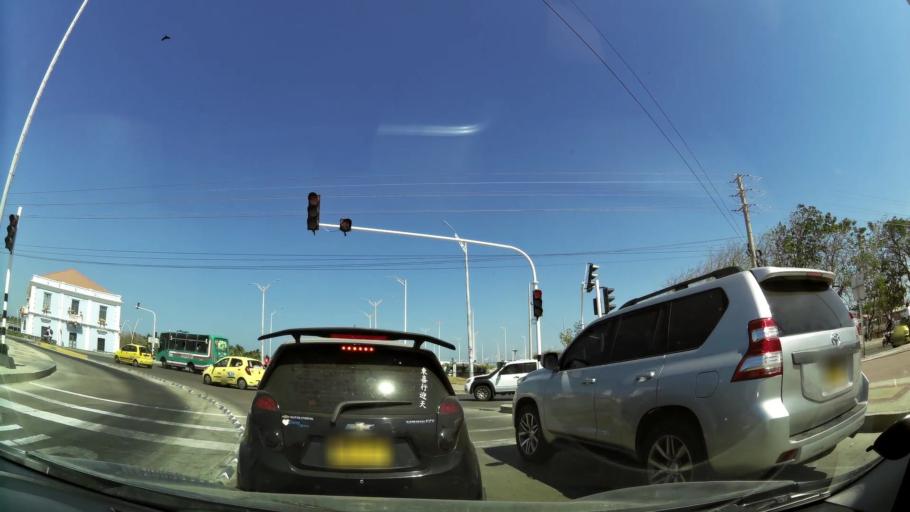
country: CO
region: Atlantico
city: Barranquilla
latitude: 10.9851
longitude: -74.7762
